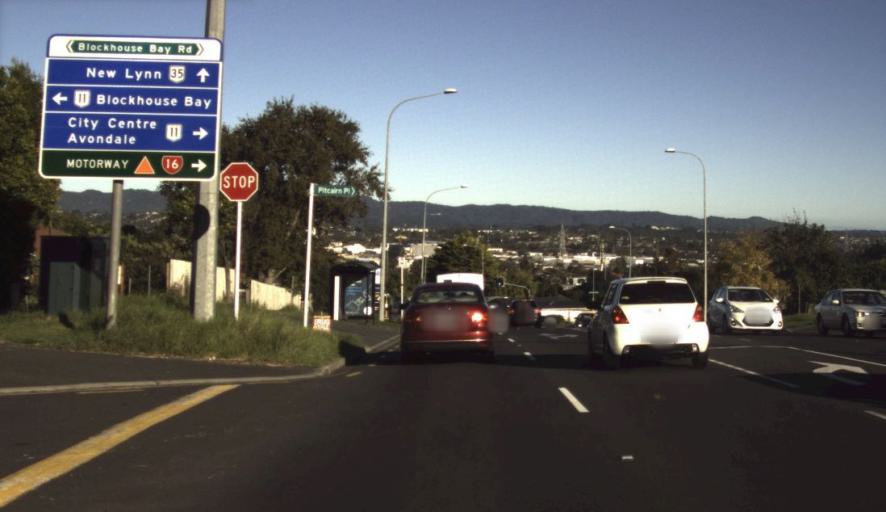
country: NZ
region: Auckland
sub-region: Auckland
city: Rosebank
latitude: -36.9060
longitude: 174.7035
